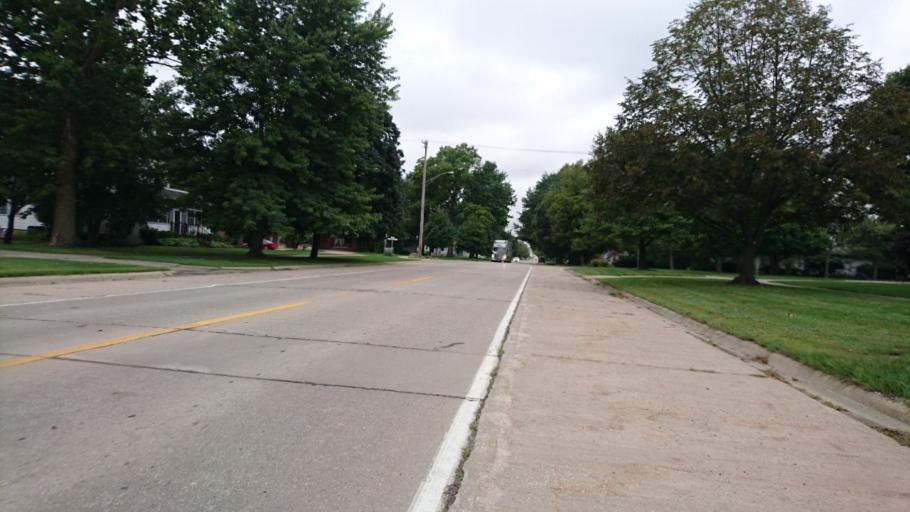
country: US
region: Illinois
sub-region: Livingston County
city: Dwight
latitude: 41.0941
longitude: -88.4311
